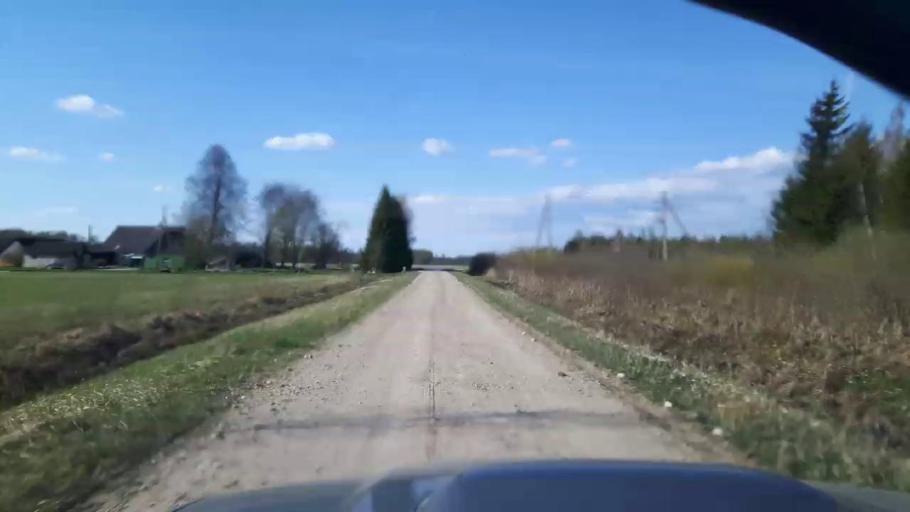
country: EE
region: Paernumaa
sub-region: Tootsi vald
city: Tootsi
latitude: 58.4316
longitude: 24.8514
